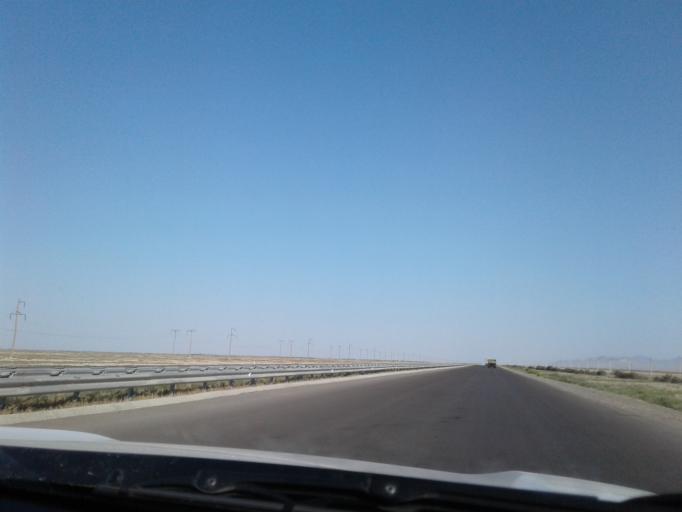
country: TM
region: Balkan
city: Serdar
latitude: 39.0564
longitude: 56.1134
